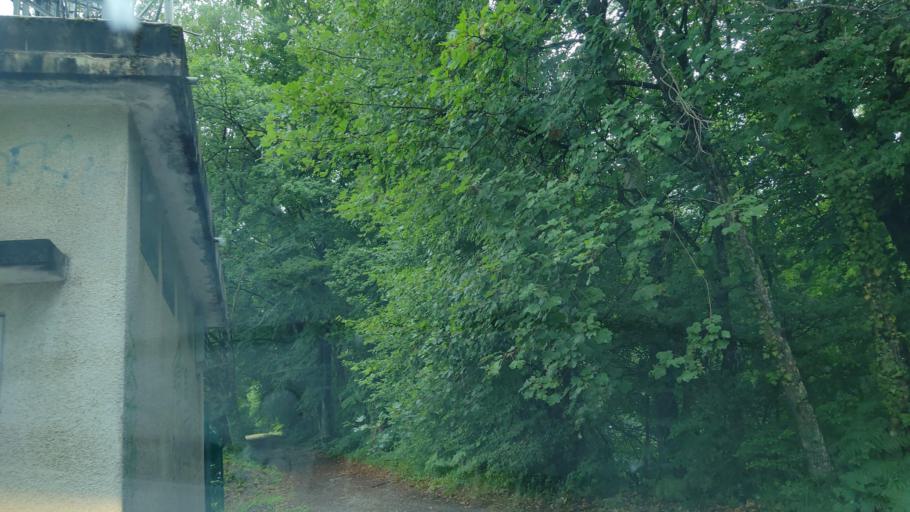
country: FR
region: Rhone-Alpes
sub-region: Departement de la Savoie
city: La Rochette
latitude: 45.4922
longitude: 6.1261
